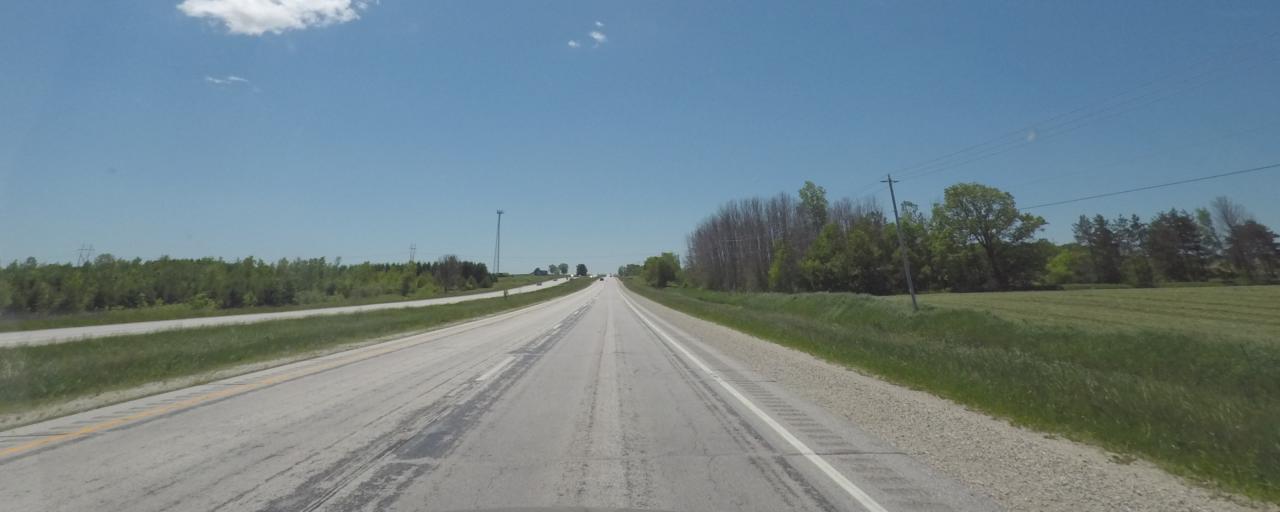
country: US
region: Wisconsin
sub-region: Sheboygan County
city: Plymouth
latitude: 43.7011
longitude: -87.9408
